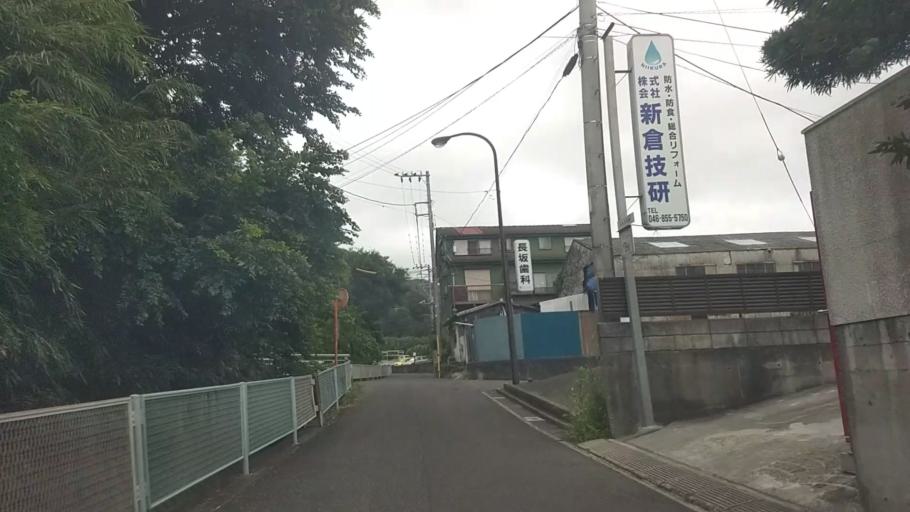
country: JP
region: Kanagawa
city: Hayama
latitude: 35.2303
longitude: 139.6242
